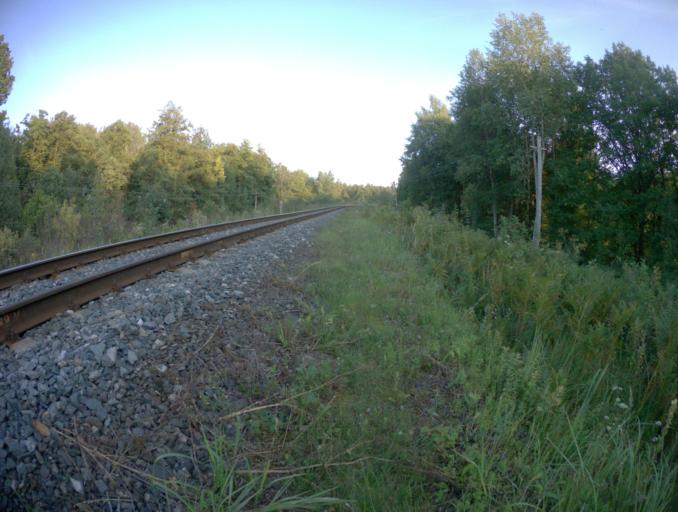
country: RU
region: Vladimir
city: Raduzhnyy
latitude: 56.0445
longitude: 40.3834
